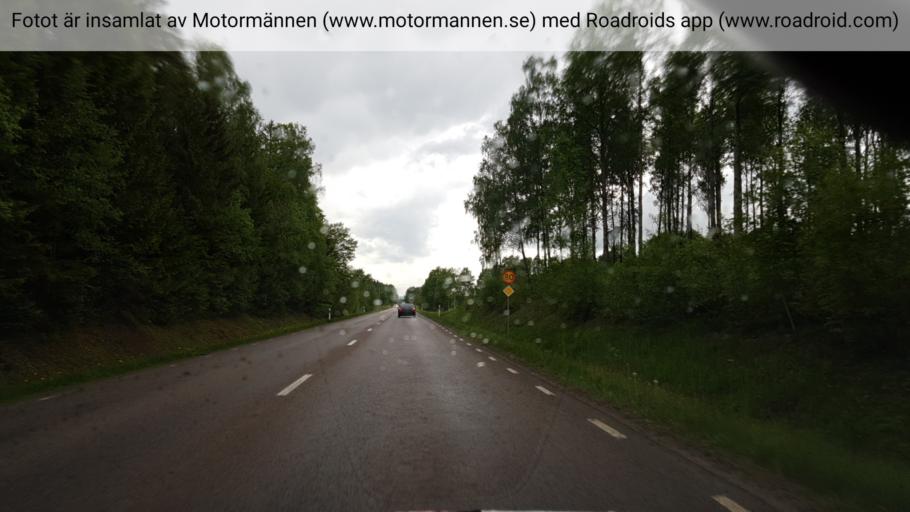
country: SE
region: Vaestra Goetaland
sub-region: Tidaholms Kommun
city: Olofstorp
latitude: 58.3647
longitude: 14.0222
